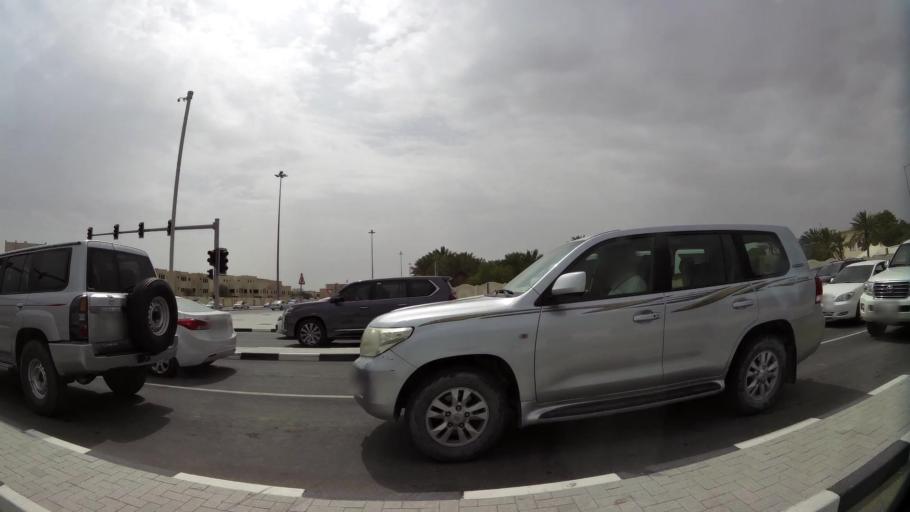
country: QA
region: Baladiyat ar Rayyan
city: Ar Rayyan
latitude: 25.3482
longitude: 51.4673
